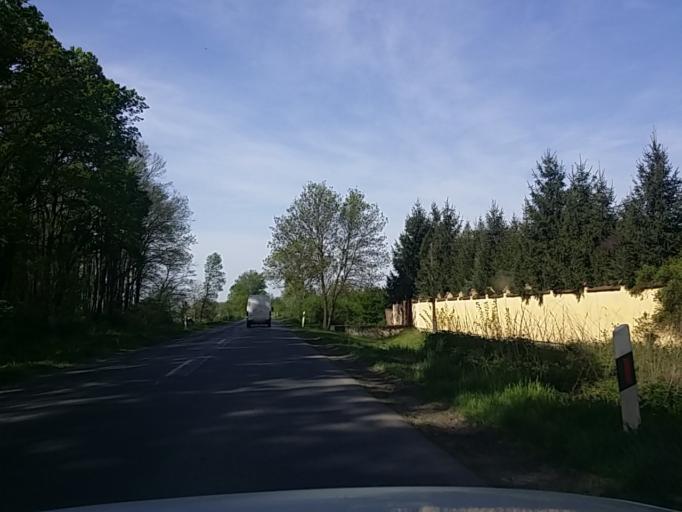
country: HU
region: Bekes
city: Doboz
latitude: 46.7180
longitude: 21.1991
